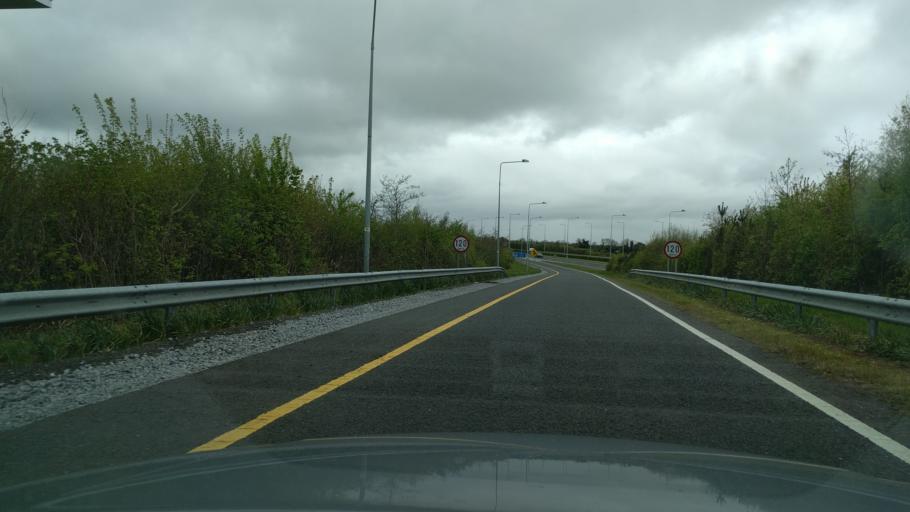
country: IE
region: Leinster
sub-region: An Mhi
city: Stamullin
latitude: 53.6390
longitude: -6.2564
